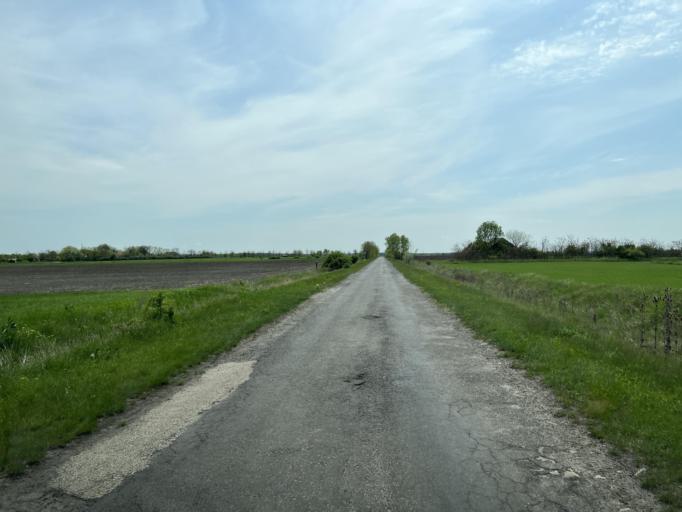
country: HU
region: Pest
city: Tapiogyorgye
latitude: 47.3044
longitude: 19.9776
